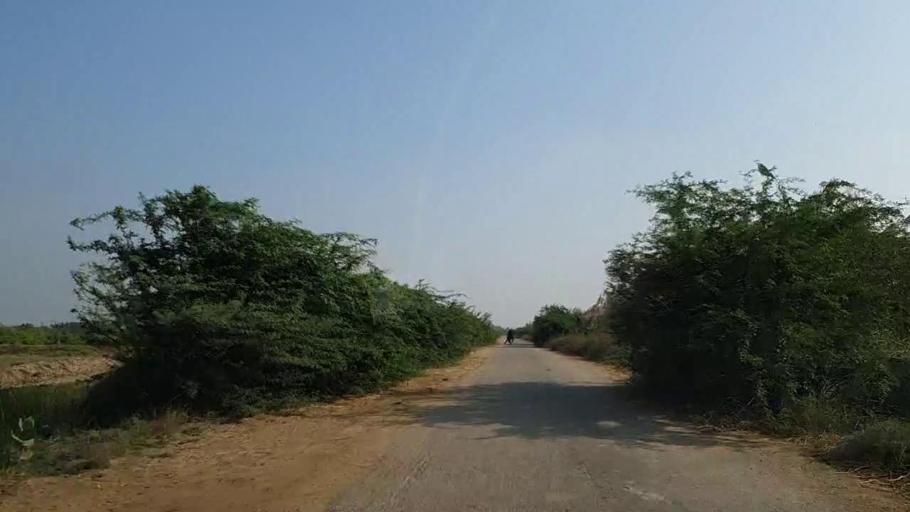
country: PK
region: Sindh
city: Mirpur Sakro
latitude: 24.6245
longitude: 67.6556
